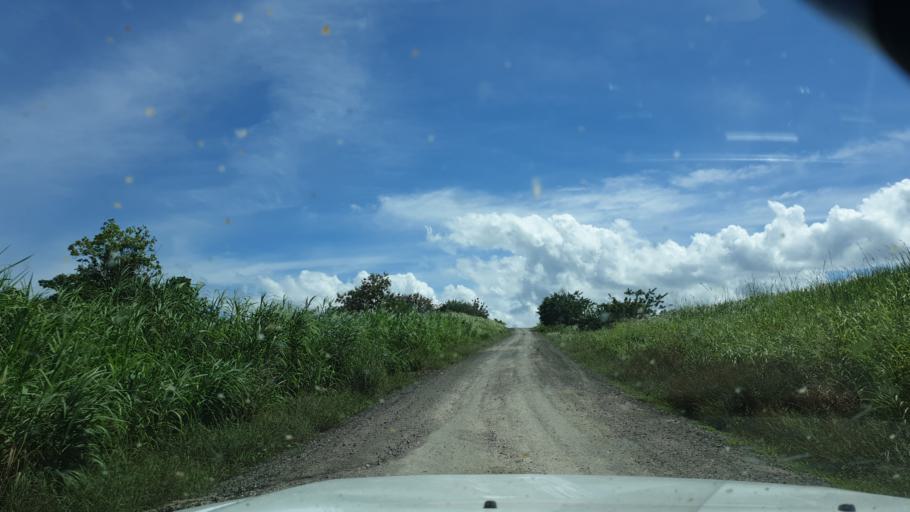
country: PG
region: Madang
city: Madang
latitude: -4.6211
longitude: 145.5603
